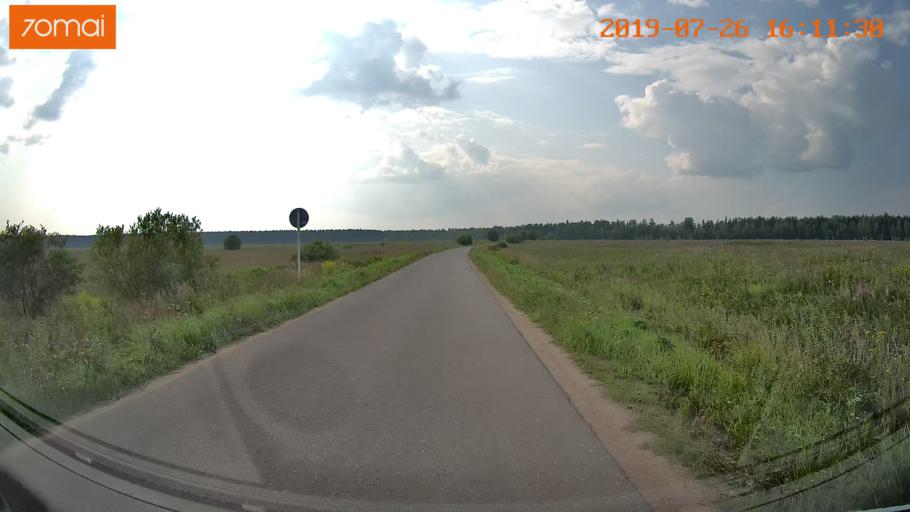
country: RU
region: Ivanovo
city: Bogorodskoye
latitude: 57.0656
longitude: 41.0600
